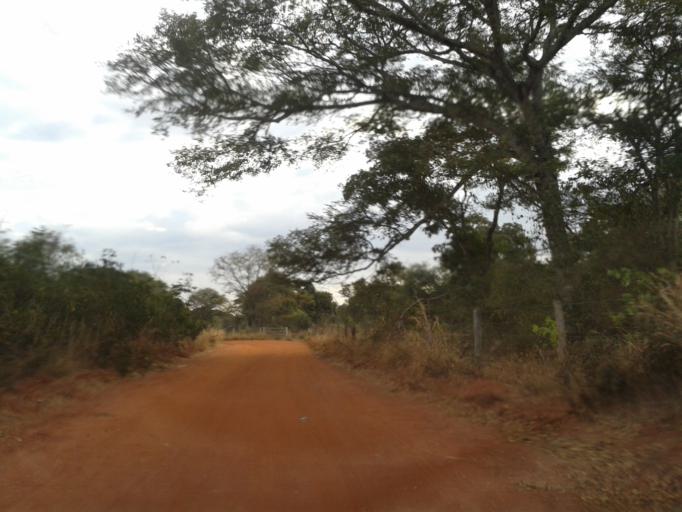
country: BR
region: Minas Gerais
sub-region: Santa Vitoria
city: Santa Vitoria
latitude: -18.7663
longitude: -50.1874
